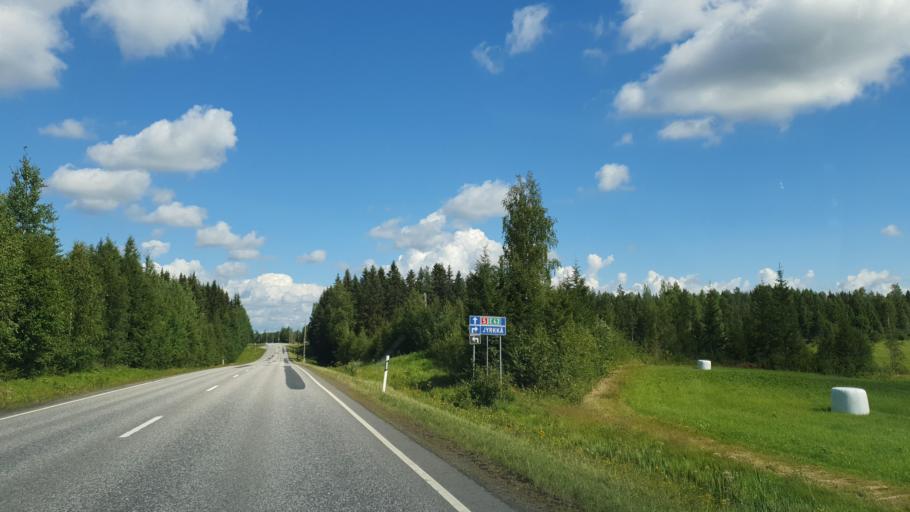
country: FI
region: Northern Savo
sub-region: Ylae-Savo
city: Sonkajaervi
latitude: 63.7220
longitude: 27.3695
